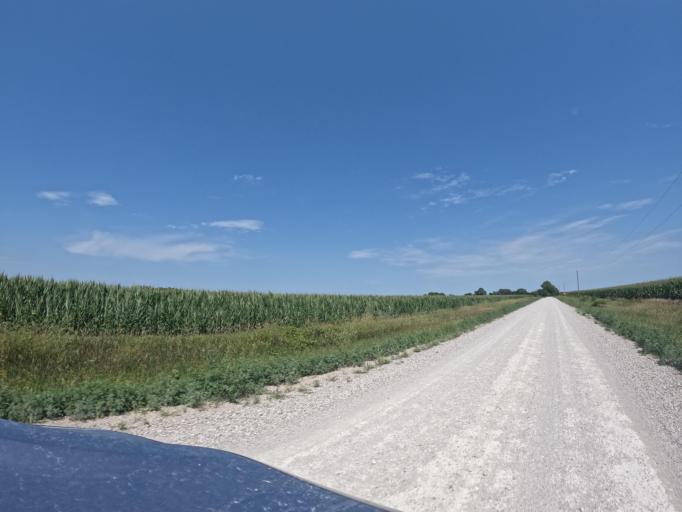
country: US
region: Iowa
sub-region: Henry County
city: Mount Pleasant
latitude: 40.8900
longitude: -91.6356
